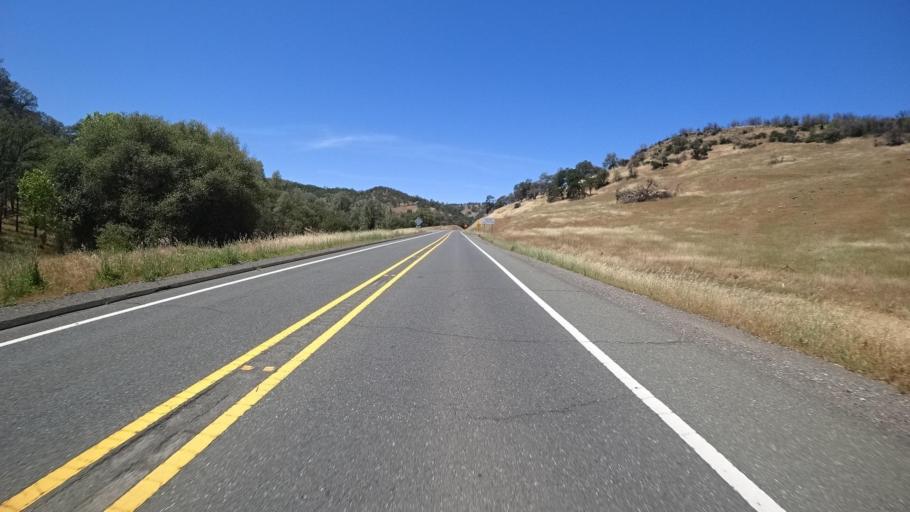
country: US
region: California
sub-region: Lake County
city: Hidden Valley Lake
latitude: 38.8258
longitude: -122.5809
